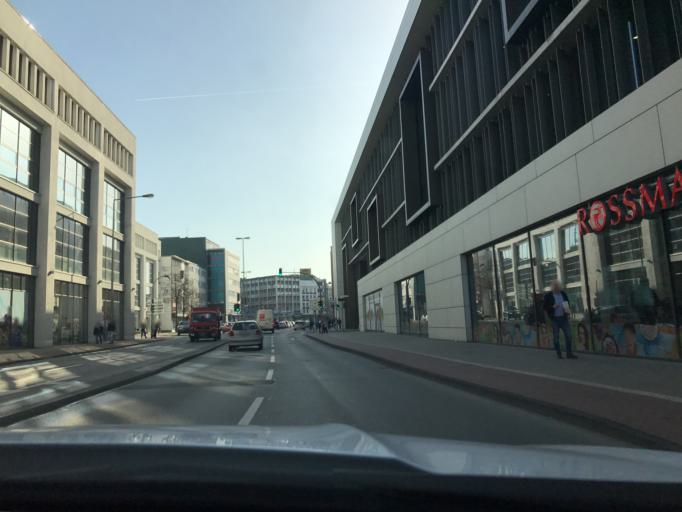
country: DE
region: North Rhine-Westphalia
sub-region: Regierungsbezirk Dusseldorf
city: Duisburg
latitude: 51.4340
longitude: 6.7620
